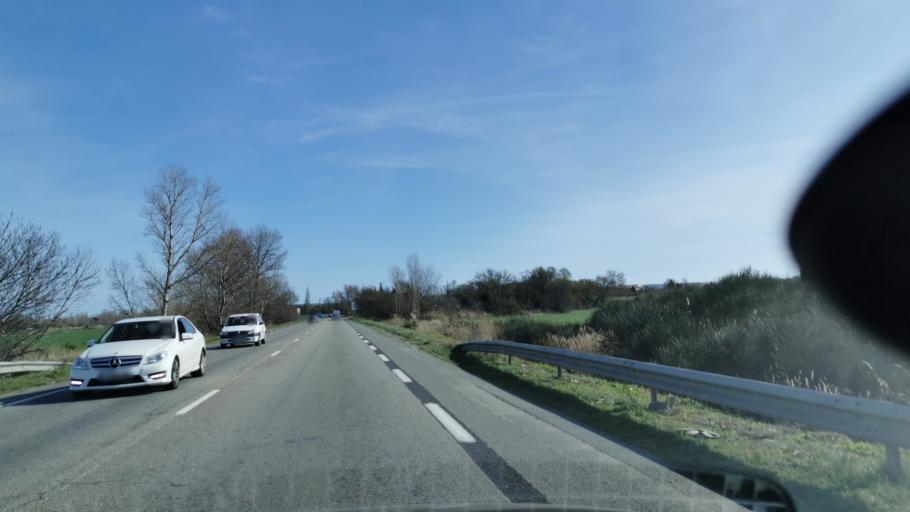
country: FR
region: Languedoc-Roussillon
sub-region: Departement de l'Aude
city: Narbonne
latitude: 43.1939
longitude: 2.9883
